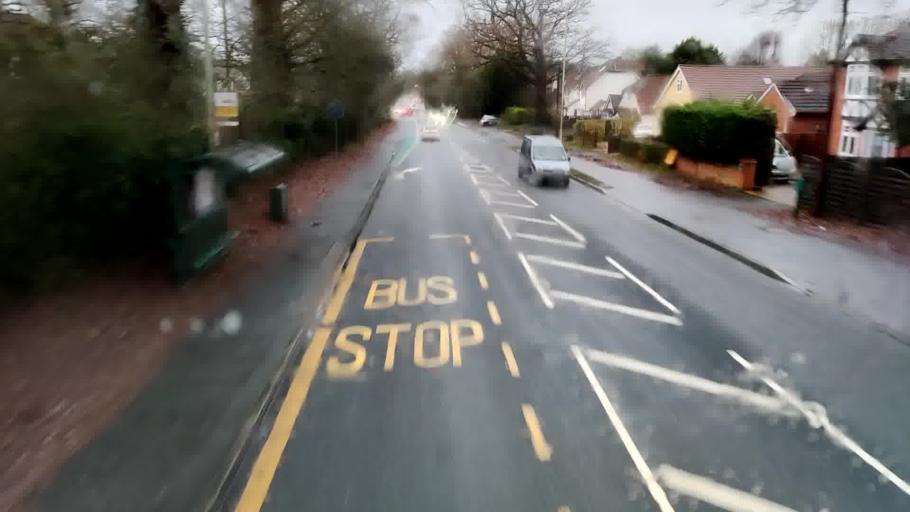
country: GB
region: England
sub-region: Wokingham
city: Wokingham
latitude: 51.4170
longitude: -0.8491
